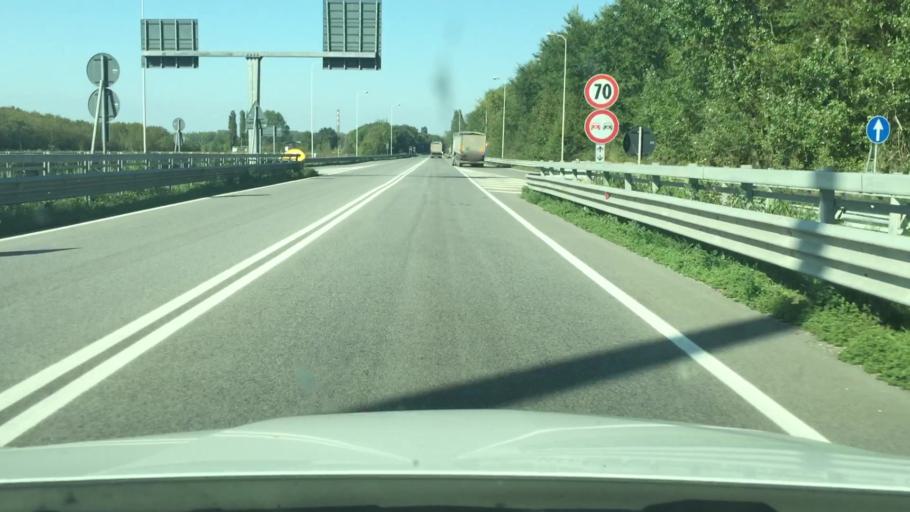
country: IT
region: Emilia-Romagna
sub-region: Provincia di Ravenna
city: Ravenna
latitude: 44.4606
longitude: 12.2089
